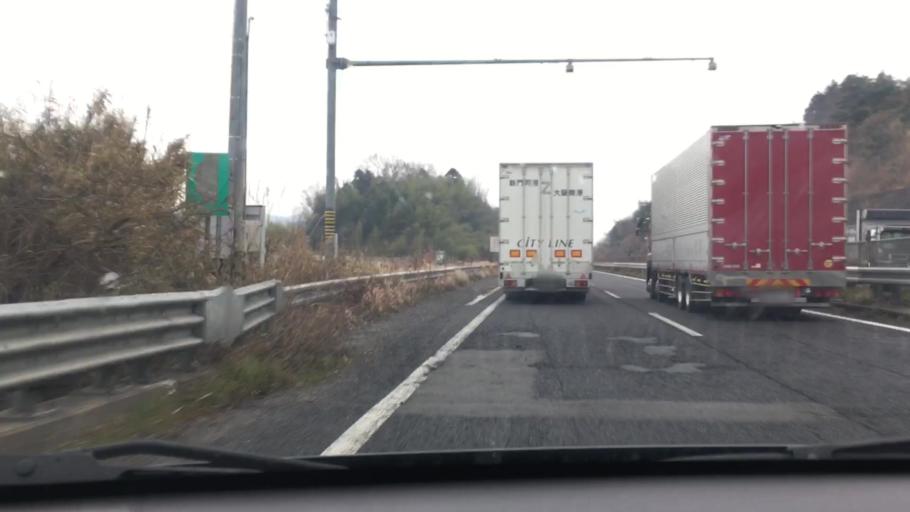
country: JP
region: Mie
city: Ueno-ebisumachi
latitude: 34.7842
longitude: 136.1593
